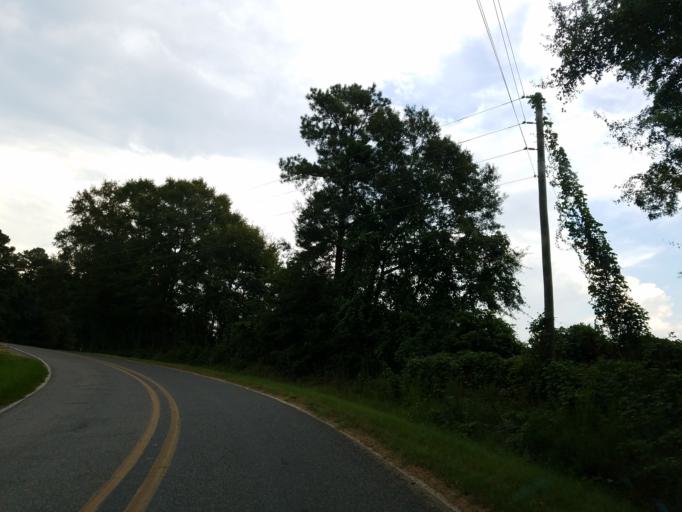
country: US
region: Mississippi
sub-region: Wayne County
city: Belmont
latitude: 31.4387
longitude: -88.4714
